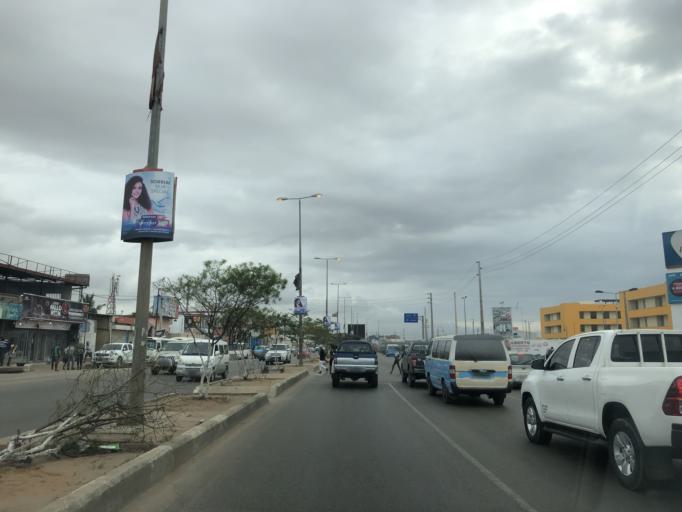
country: AO
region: Luanda
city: Luanda
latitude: -8.8799
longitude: 13.2094
